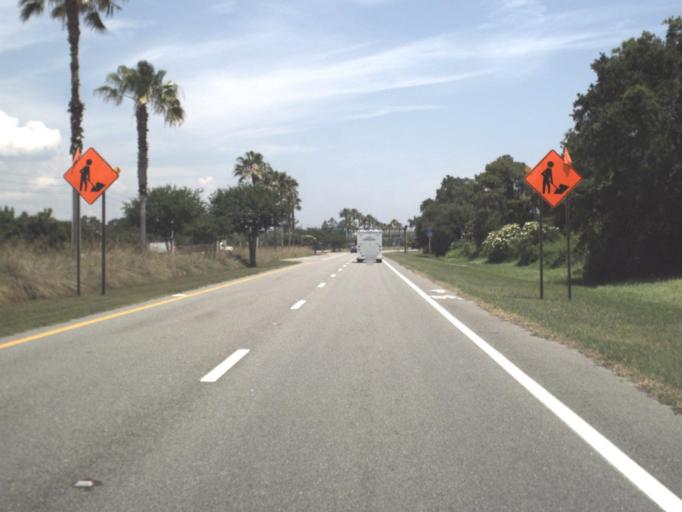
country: US
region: Florida
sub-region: Saint Johns County
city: Sawgrass
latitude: 30.1926
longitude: -81.3802
